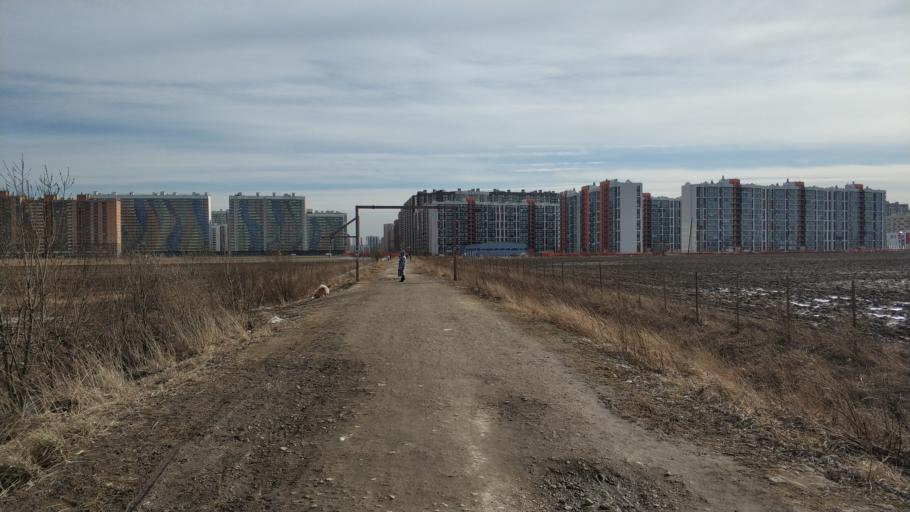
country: RU
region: Leningrad
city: Bugry
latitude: 60.0620
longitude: 30.4105
